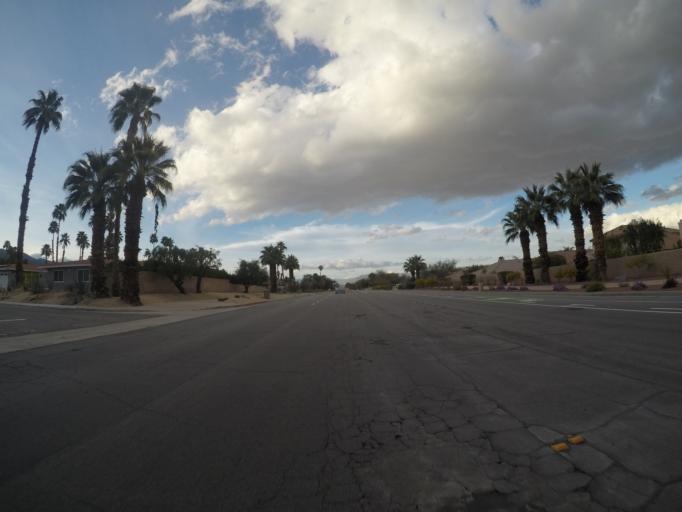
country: US
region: California
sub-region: Riverside County
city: Palm Springs
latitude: 33.8056
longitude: -116.5107
